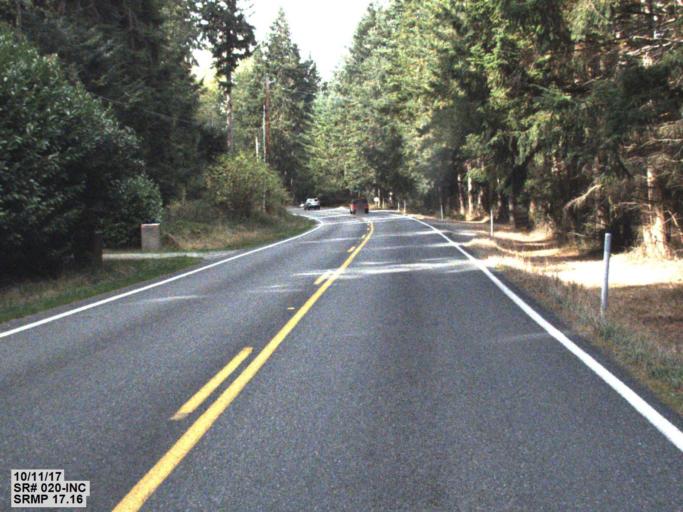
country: US
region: Washington
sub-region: Island County
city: Coupeville
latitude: 48.1797
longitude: -122.6202
